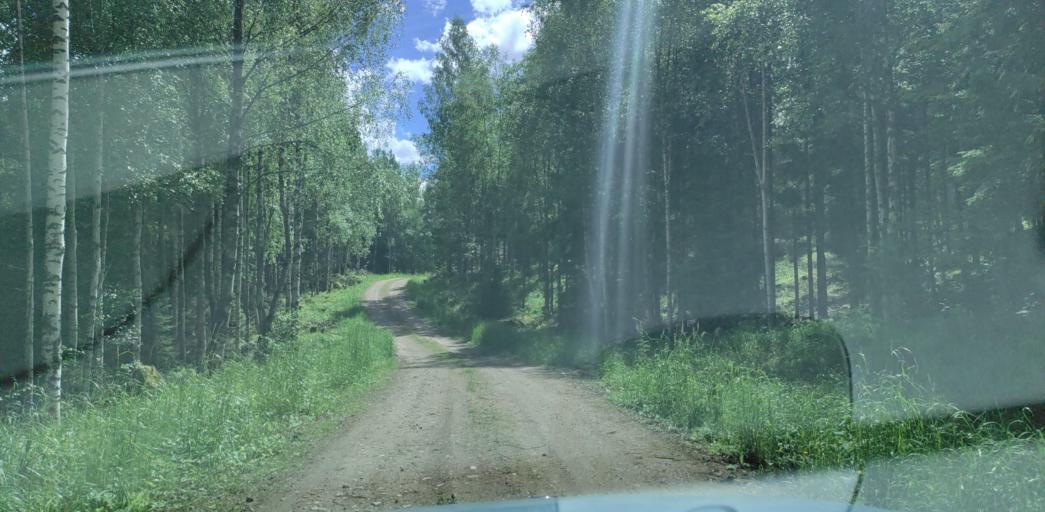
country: SE
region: Vaermland
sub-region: Hagfors Kommun
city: Ekshaerad
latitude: 60.1177
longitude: 13.3257
